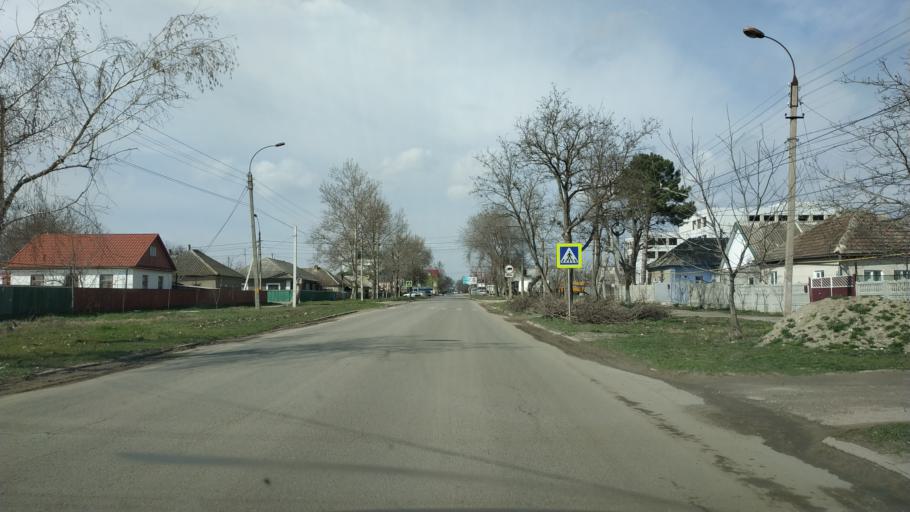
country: MD
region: Gagauzia
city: Vulcanesti
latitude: 45.6797
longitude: 28.4093
